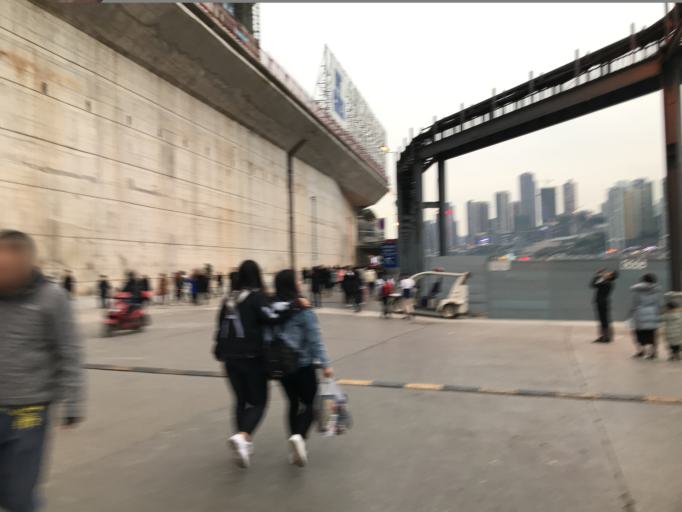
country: CN
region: Chongqing Shi
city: Nanping
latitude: 29.5675
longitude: 106.5854
